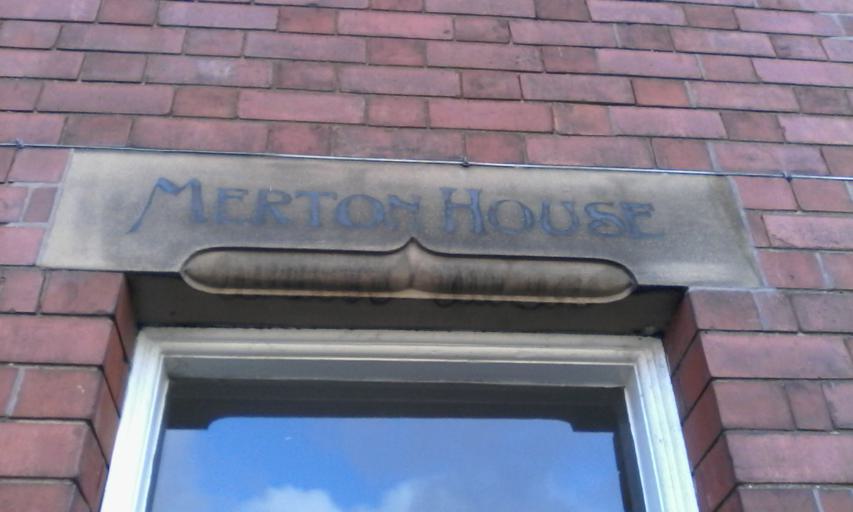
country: GB
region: England
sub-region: Nottinghamshire
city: Arnold
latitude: 52.9827
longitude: -1.1201
